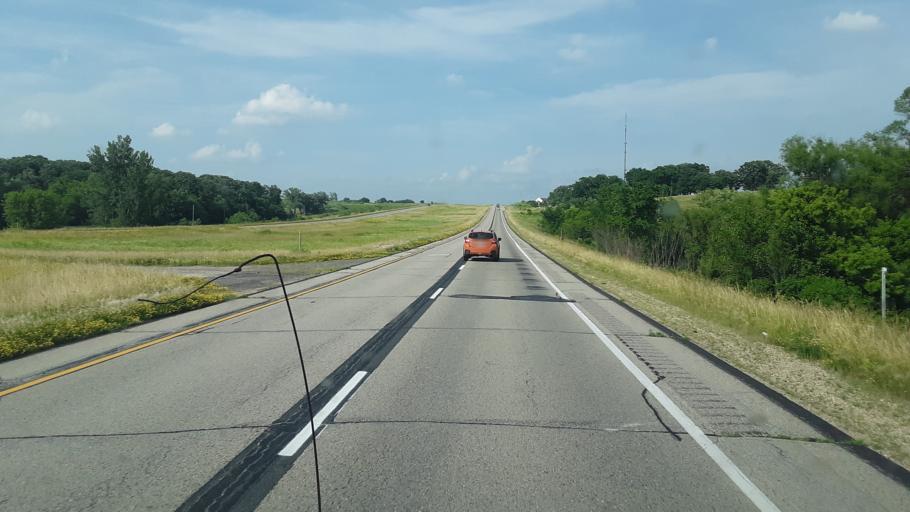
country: US
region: Iowa
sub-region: Jasper County
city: Baxter
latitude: 41.8733
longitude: -93.2176
